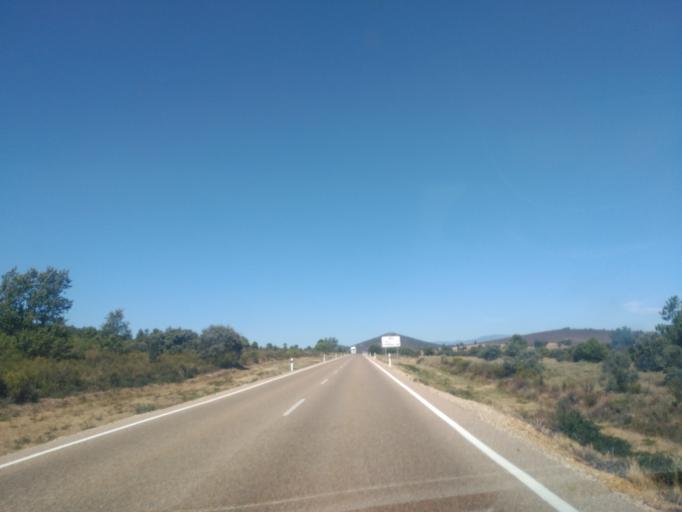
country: ES
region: Castille and Leon
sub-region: Provincia de Zamora
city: Otero de Bodas
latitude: 41.9291
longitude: -6.1121
